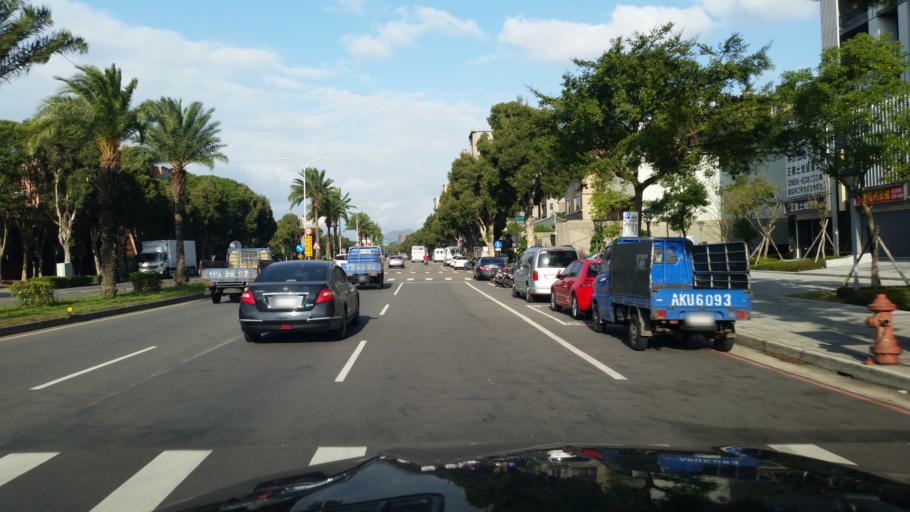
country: TW
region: Taiwan
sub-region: Taoyuan
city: Taoyuan
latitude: 25.0764
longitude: 121.3647
